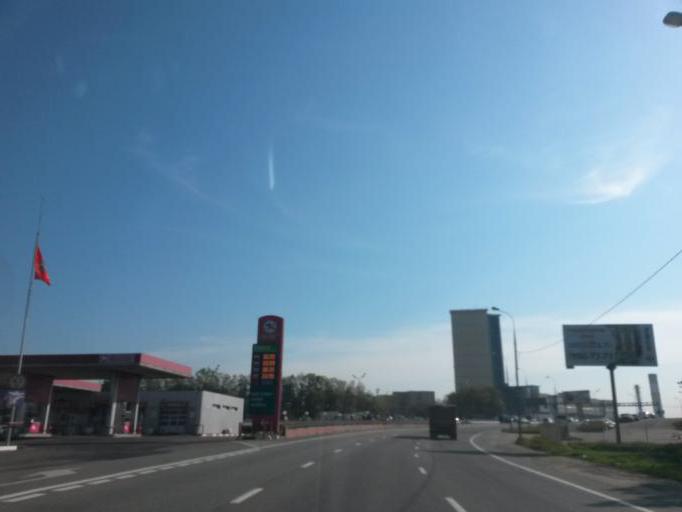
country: RU
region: Moscow
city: Annino
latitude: 55.5745
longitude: 37.6045
